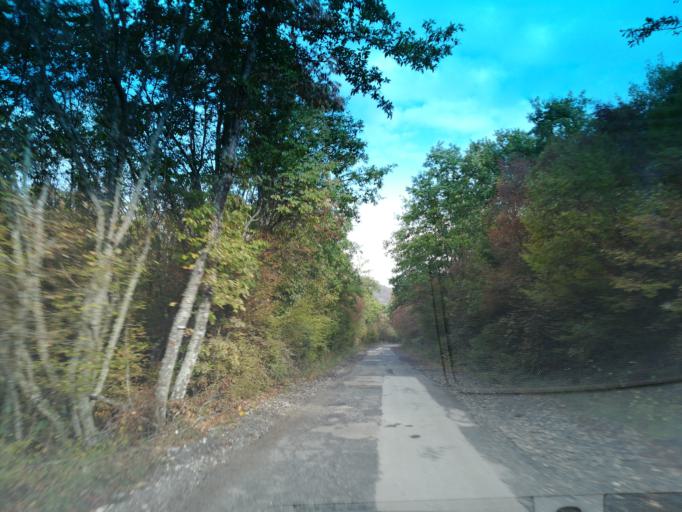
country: BG
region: Stara Zagora
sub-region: Obshtina Nikolaevo
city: Elkhovo
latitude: 42.3246
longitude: 25.3986
